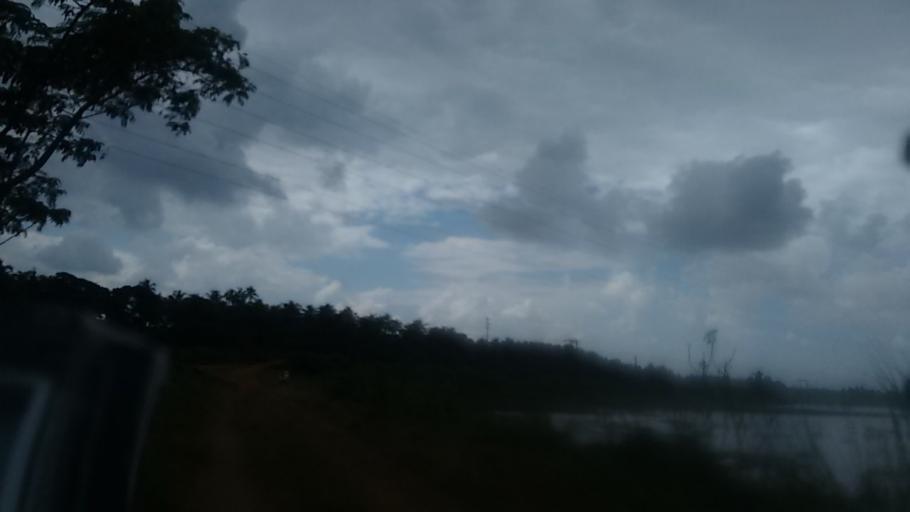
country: IN
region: Kerala
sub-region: Thrissur District
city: Trichur
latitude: 10.5284
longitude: 76.1664
